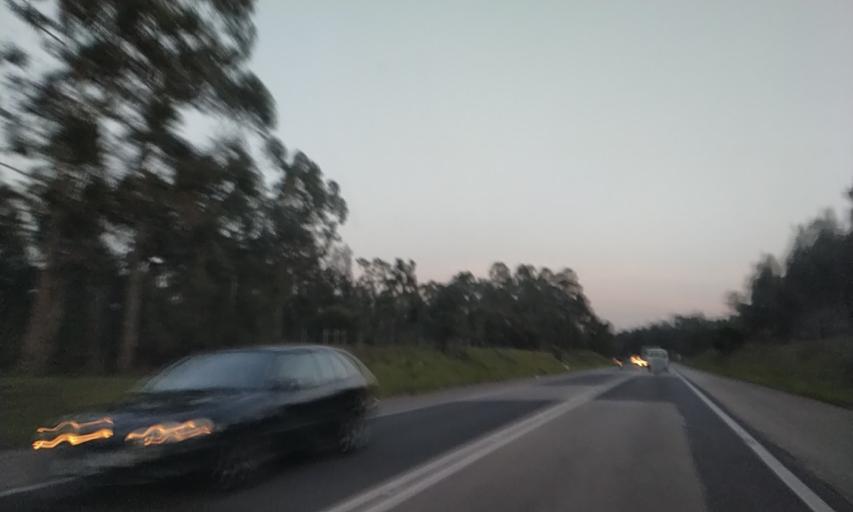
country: PT
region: Leiria
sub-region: Leiria
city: Leiria
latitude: 39.7445
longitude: -8.8473
